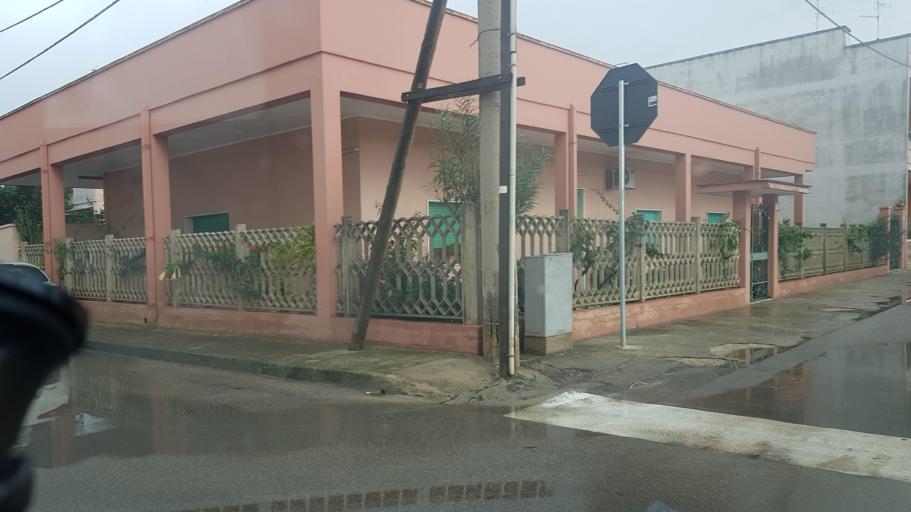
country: IT
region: Apulia
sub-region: Provincia di Lecce
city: Carmiano
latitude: 40.3374
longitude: 18.0438
